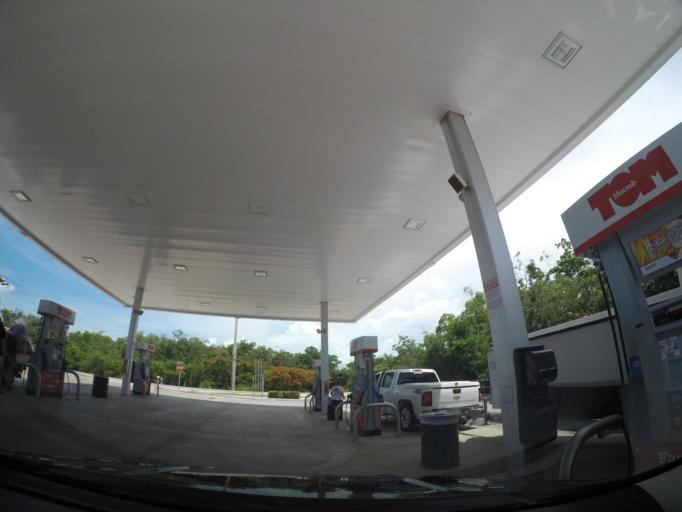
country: US
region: Florida
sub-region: Monroe County
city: Key Largo
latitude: 25.0776
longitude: -80.4589
